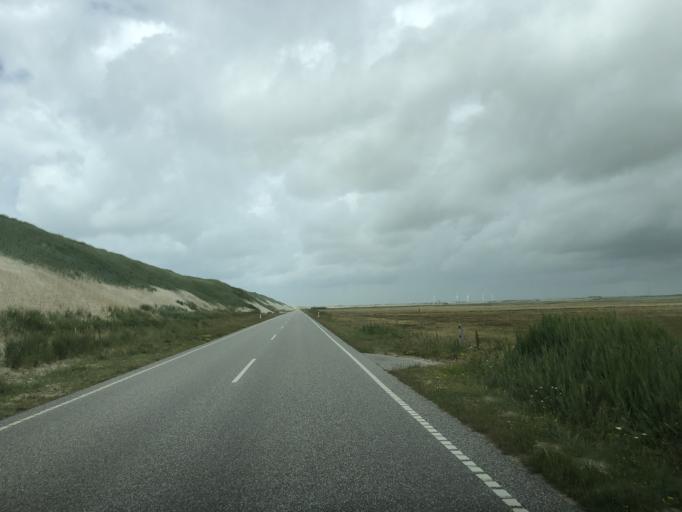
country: DK
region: Central Jutland
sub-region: Lemvig Kommune
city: Harboore
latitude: 56.4352
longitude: 8.1243
